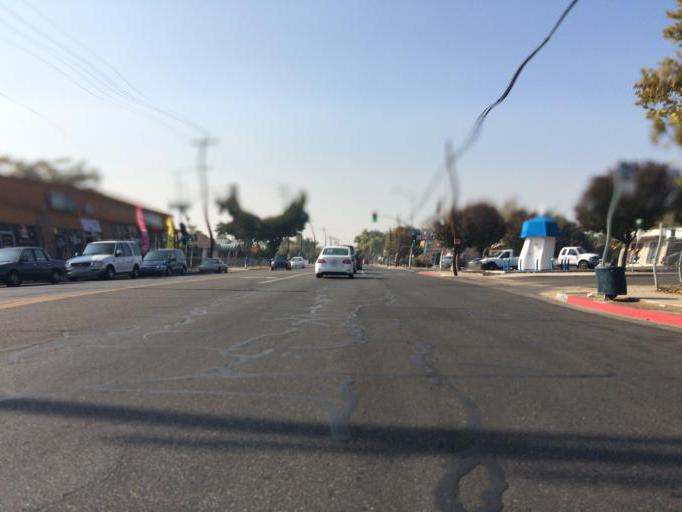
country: US
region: California
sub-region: Fresno County
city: Fresno
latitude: 36.7287
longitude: -119.7674
